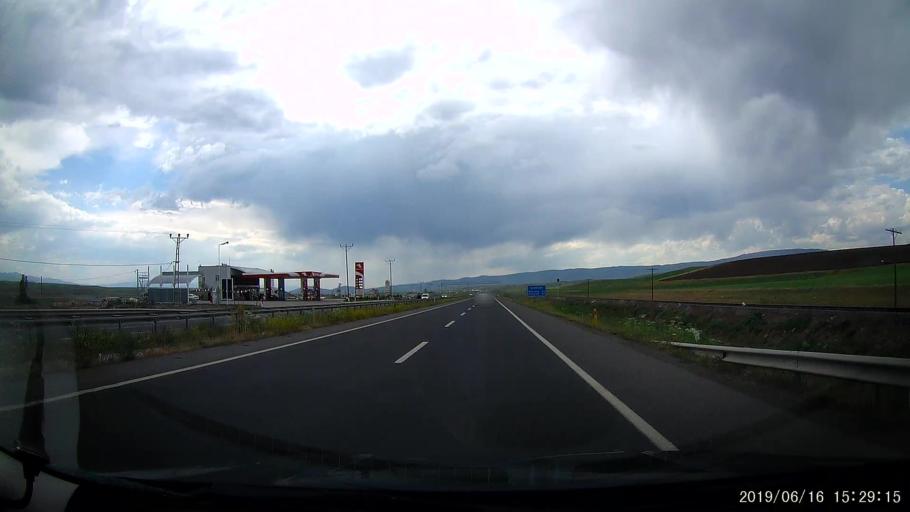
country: TR
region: Erzurum
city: Horasan
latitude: 40.0317
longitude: 42.1363
